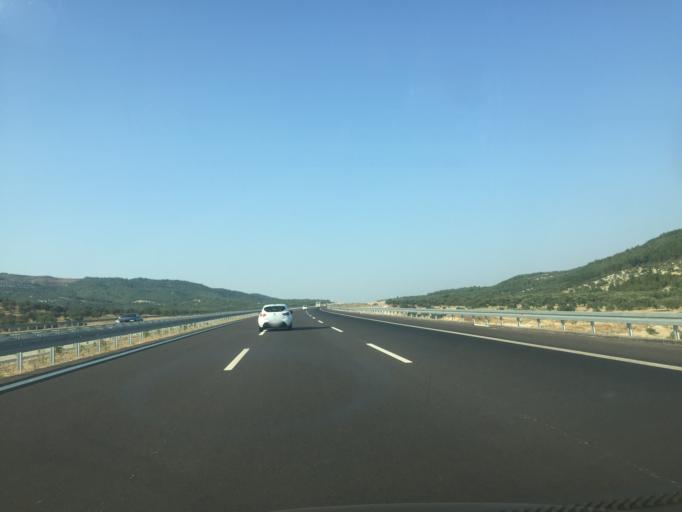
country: TR
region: Manisa
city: Zeytinliova
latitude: 38.9898
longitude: 27.7333
